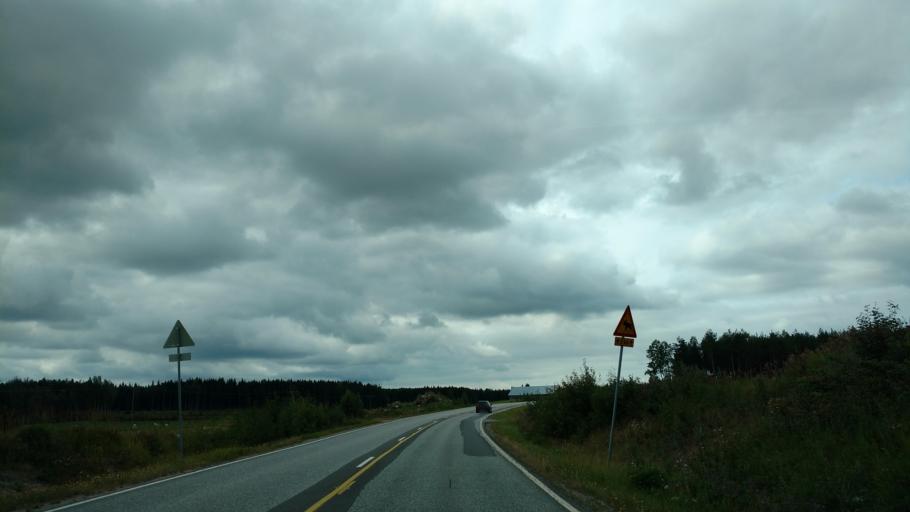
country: FI
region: Varsinais-Suomi
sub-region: Aboland-Turunmaa
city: Vaestanfjaerd
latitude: 60.1047
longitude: 22.5904
